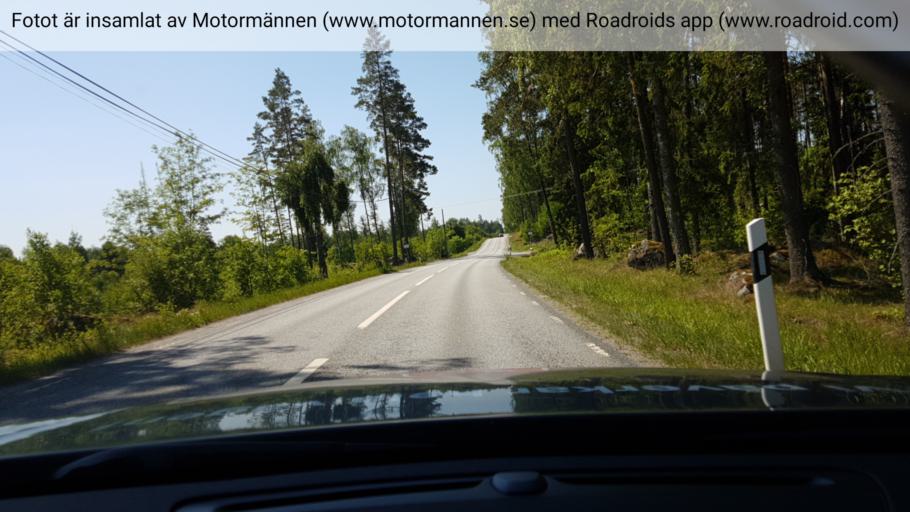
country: SE
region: Stockholm
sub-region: Norrtalje Kommun
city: Rimbo
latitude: 59.7729
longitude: 18.4324
